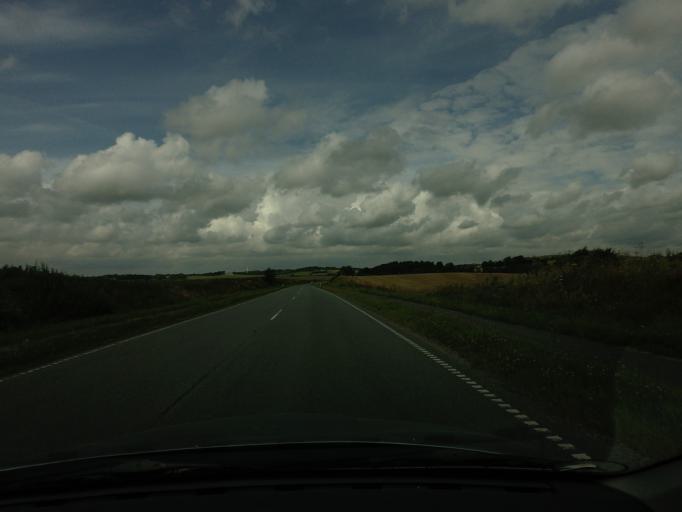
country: DK
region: North Denmark
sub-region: Hjorring Kommune
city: Tars
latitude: 57.3683
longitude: 10.1800
